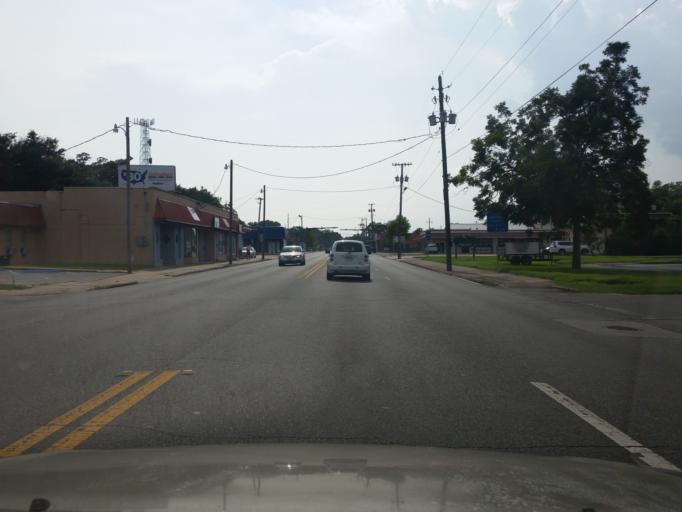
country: US
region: Florida
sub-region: Escambia County
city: Pensacola
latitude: 30.4210
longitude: -87.2444
